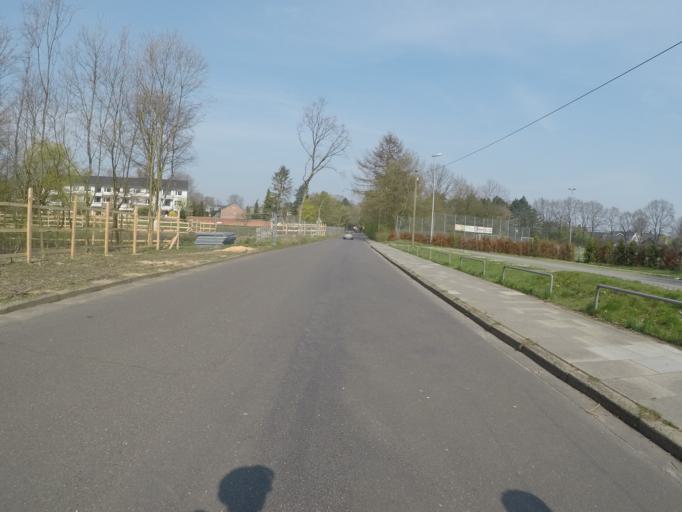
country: DE
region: Hamburg
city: Sasel
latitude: 53.6605
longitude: 10.0994
